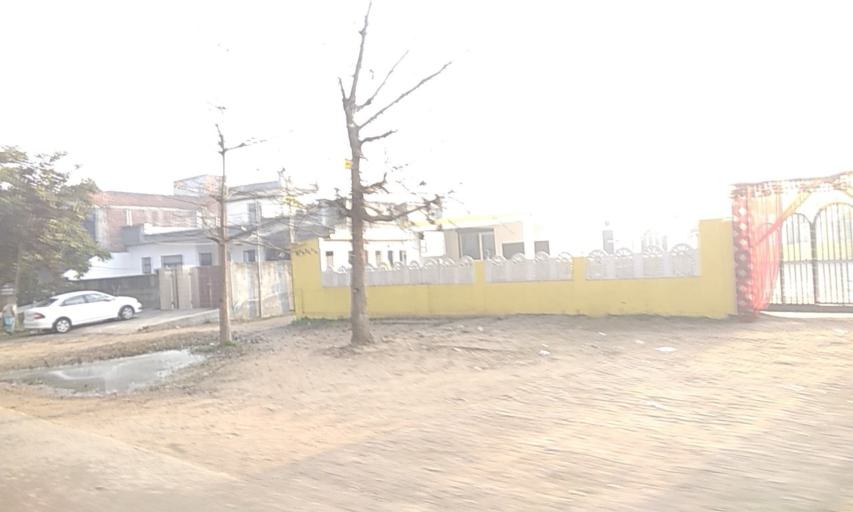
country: IN
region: Punjab
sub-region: Gurdaspur
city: Dhariwal
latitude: 31.9433
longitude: 75.3131
